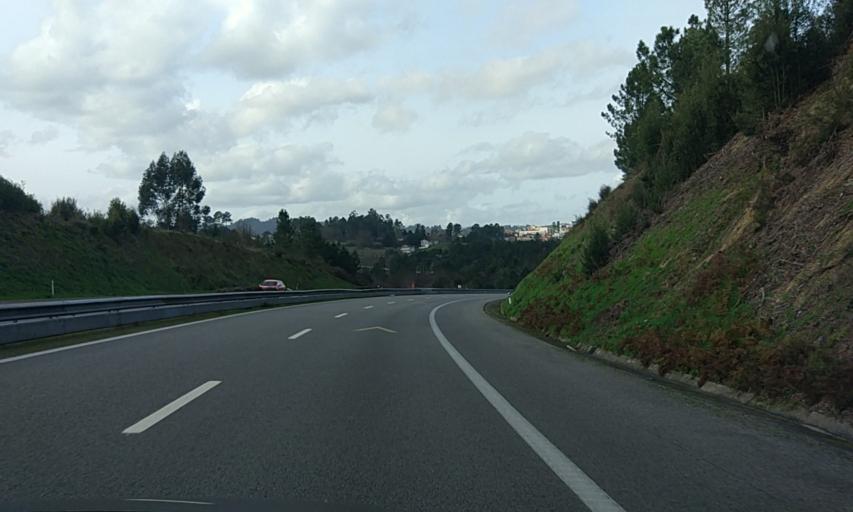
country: PT
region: Porto
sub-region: Marco de Canaveses
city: Marco de Canavezes
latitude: 41.2237
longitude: -8.1655
